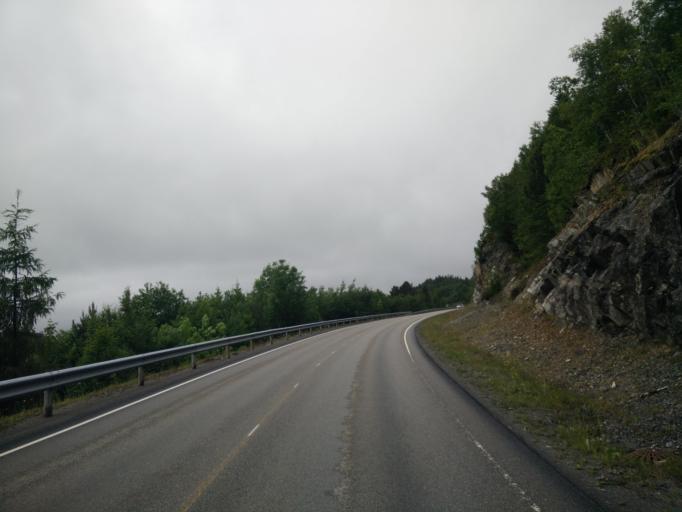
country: NO
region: More og Romsdal
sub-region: Kristiansund
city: Rensvik
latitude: 63.0063
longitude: 7.9600
